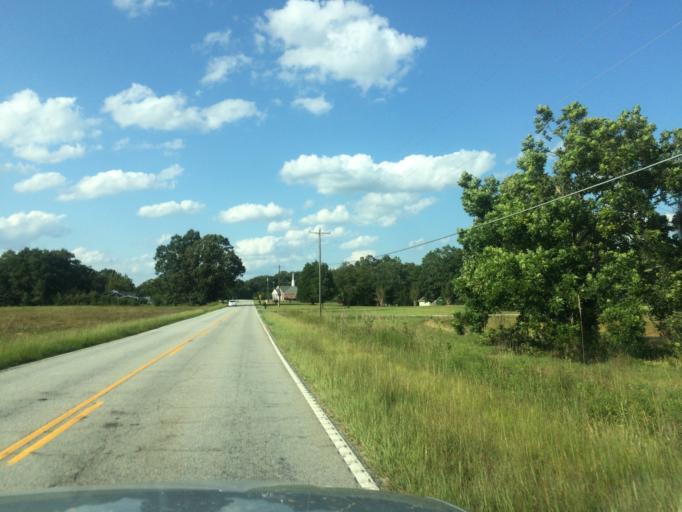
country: US
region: South Carolina
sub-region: Greenville County
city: Fountain Inn
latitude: 34.5410
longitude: -82.2001
